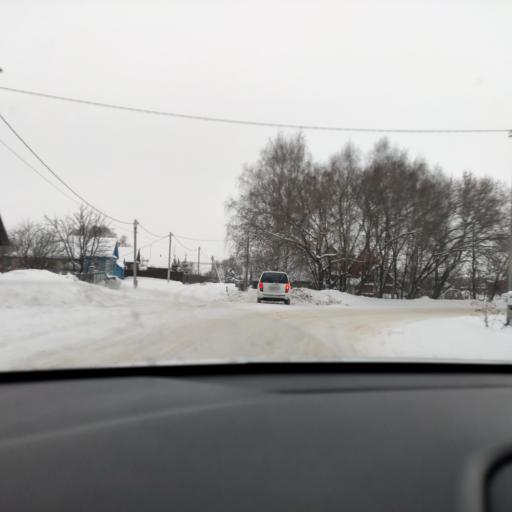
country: RU
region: Tatarstan
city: Vysokaya Gora
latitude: 55.9691
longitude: 49.1767
